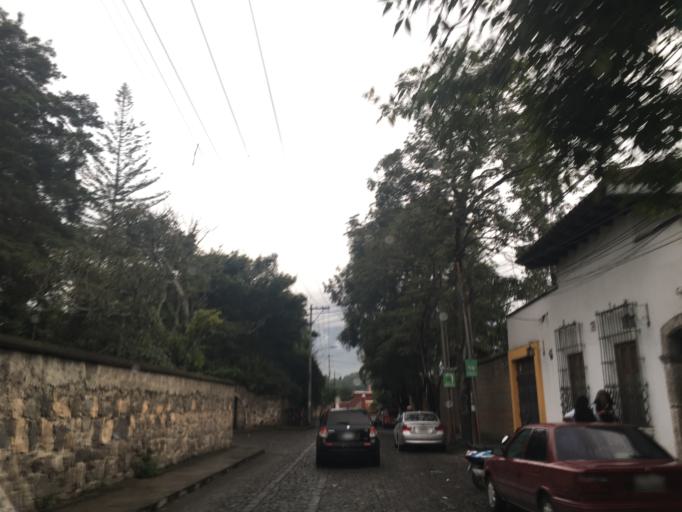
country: GT
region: Sacatepequez
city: Antigua Guatemala
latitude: 14.5556
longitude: -90.7401
